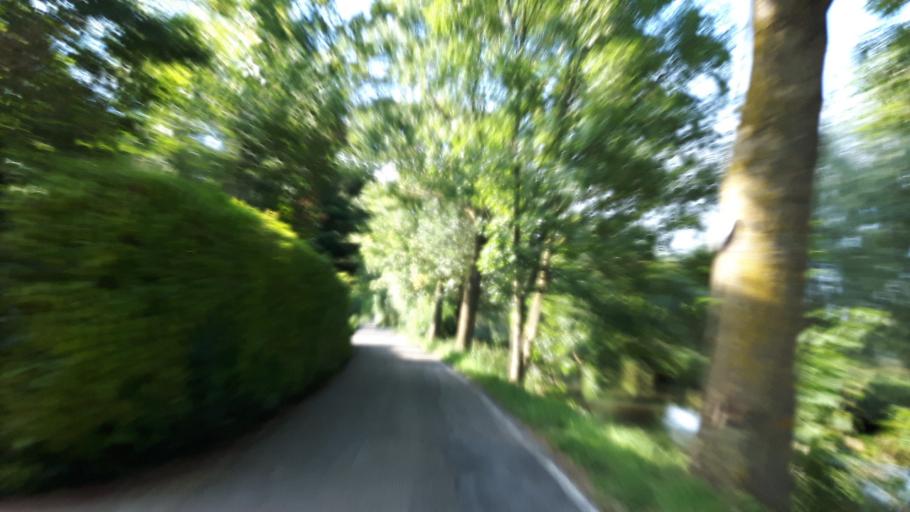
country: NL
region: Utrecht
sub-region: Gemeente Oudewater
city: Oudewater
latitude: 52.0344
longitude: 4.8858
